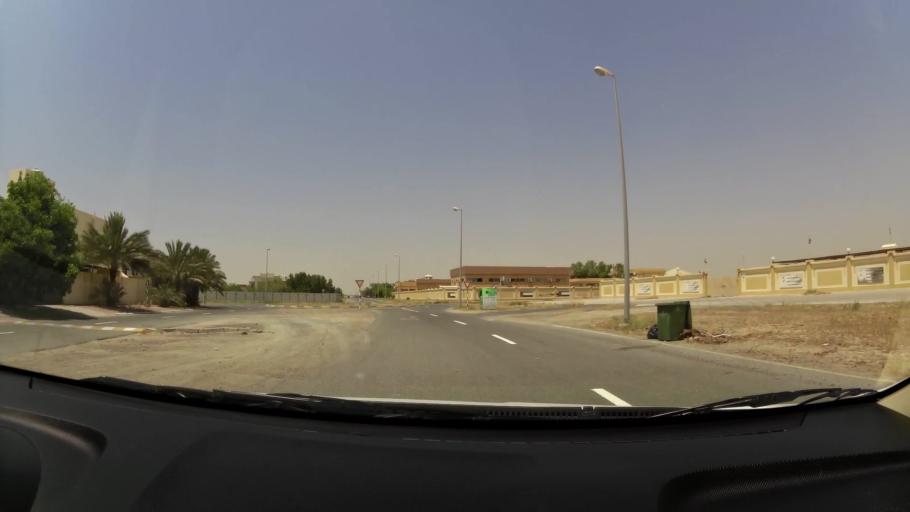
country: AE
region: Ajman
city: Ajman
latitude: 25.4261
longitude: 55.5094
